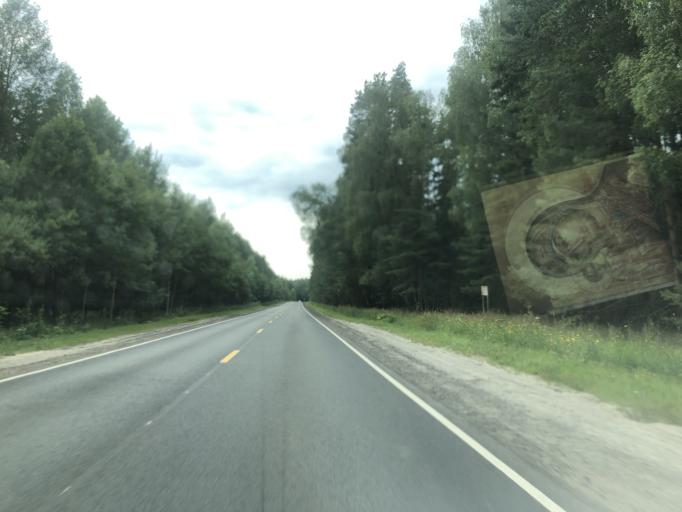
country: RU
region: Ivanovo
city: Verkhniy Landekh
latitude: 56.7398
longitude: 42.5380
